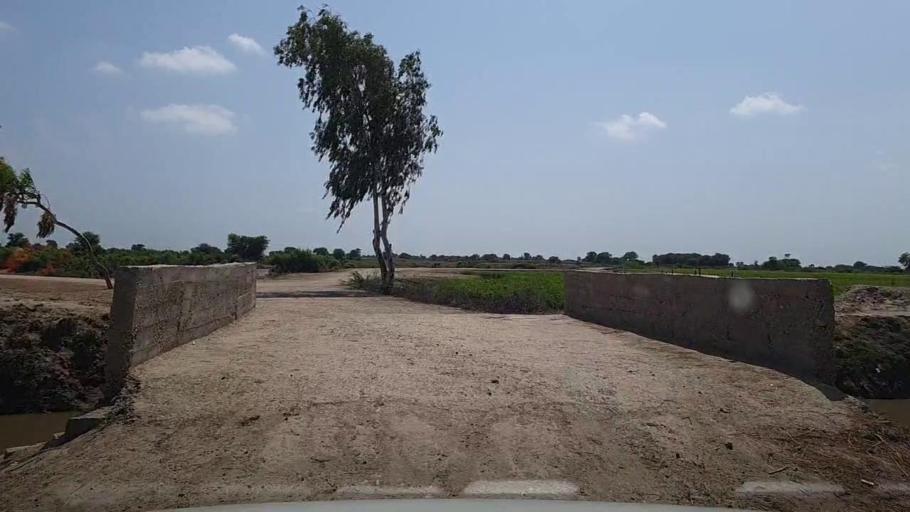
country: PK
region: Sindh
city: Kario
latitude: 24.8199
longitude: 68.6960
